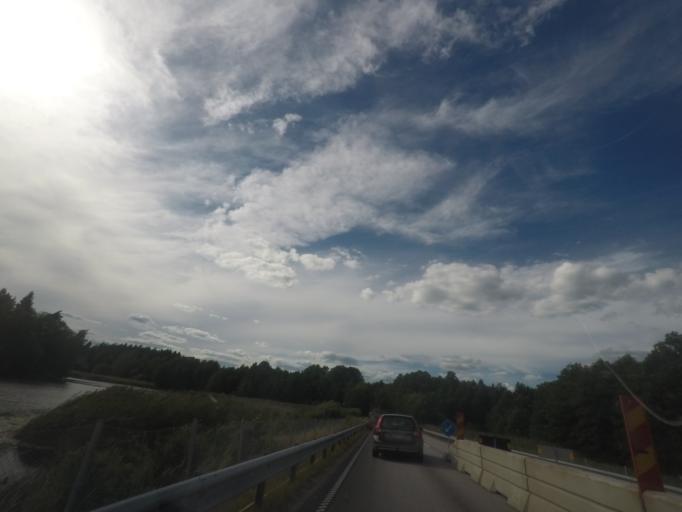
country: SE
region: Stockholm
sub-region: Norrtalje Kommun
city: Skanninge
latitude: 59.9031
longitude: 18.5897
